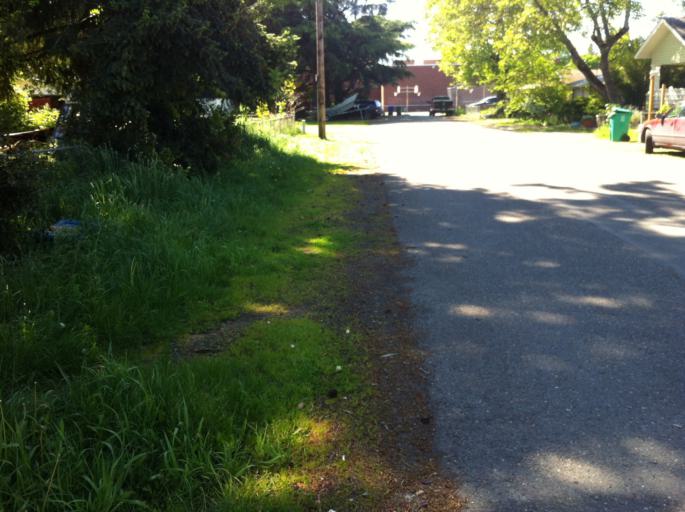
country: US
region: Oregon
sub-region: Multnomah County
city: Lents
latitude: 45.4988
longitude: -122.5900
